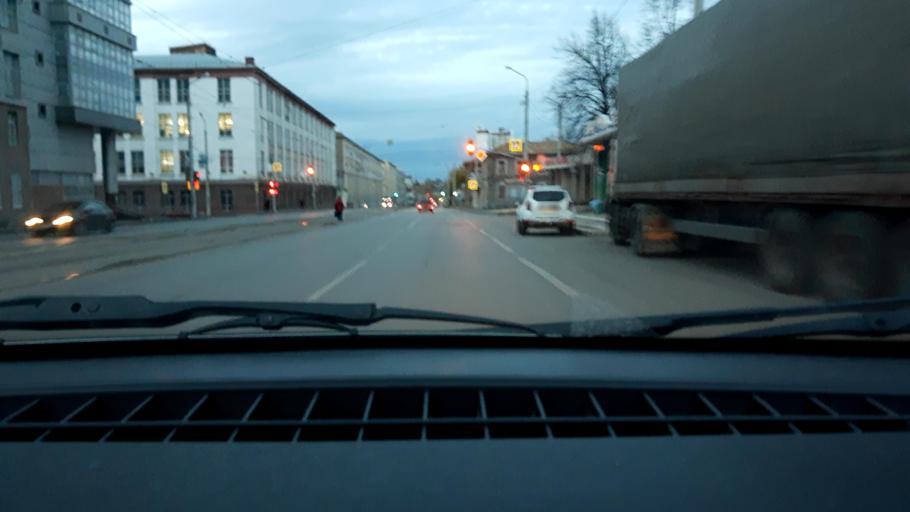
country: RU
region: Bashkortostan
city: Ufa
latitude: 54.7322
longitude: 55.9377
